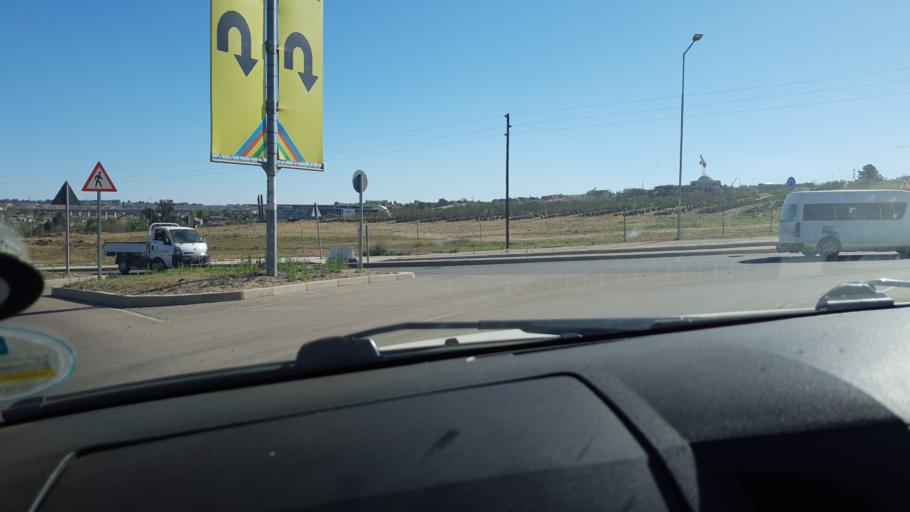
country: ZA
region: Gauteng
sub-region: City of Johannesburg Metropolitan Municipality
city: Diepsloot
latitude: -25.9767
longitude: 28.0199
